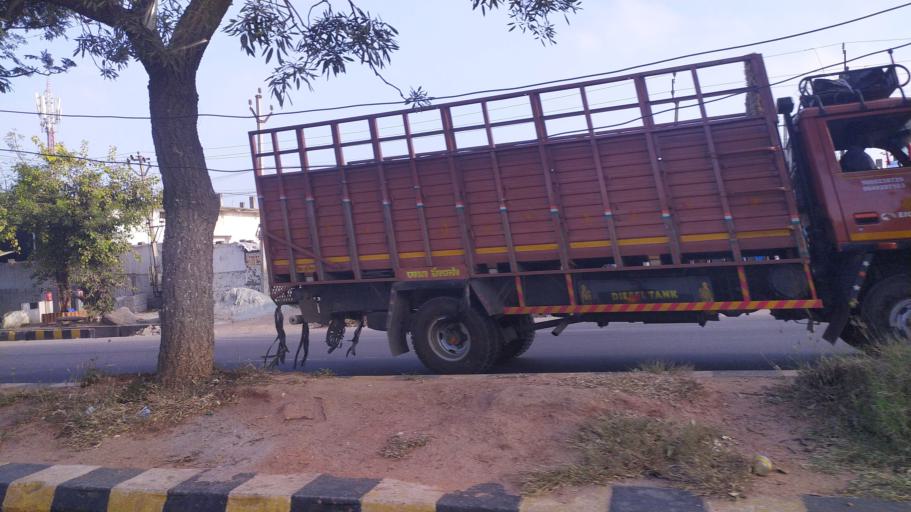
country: IN
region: Telangana
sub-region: Rangareddi
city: Balapur
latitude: 17.3180
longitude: 78.4374
